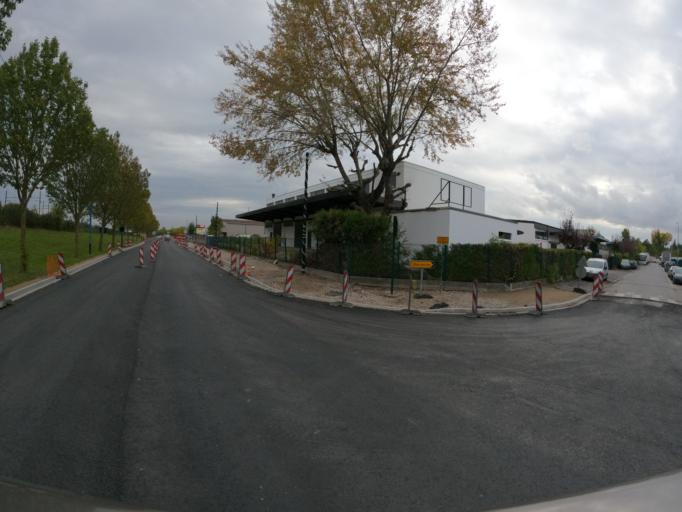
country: FR
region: Ile-de-France
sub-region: Departement de Seine-et-Marne
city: Chelles
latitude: 48.8709
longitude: 2.6022
